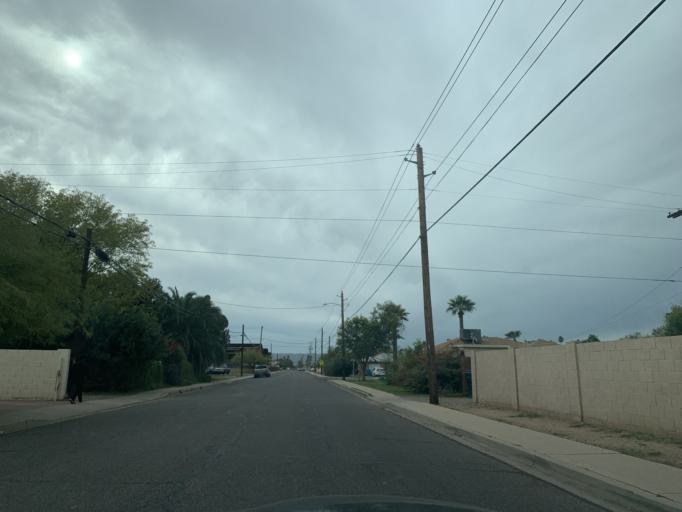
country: US
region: Arizona
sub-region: Maricopa County
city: Phoenix
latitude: 33.4719
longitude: -112.0498
